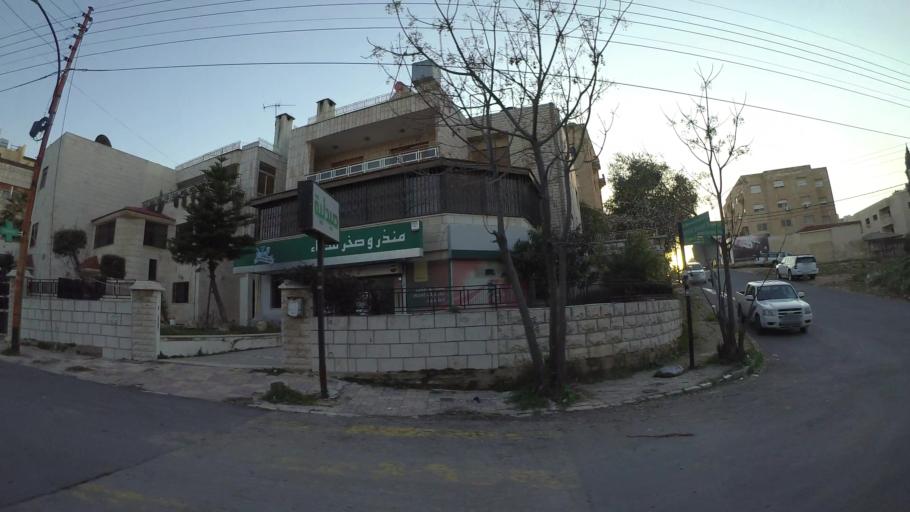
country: JO
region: Amman
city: Al Jubayhah
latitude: 31.9973
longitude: 35.8792
